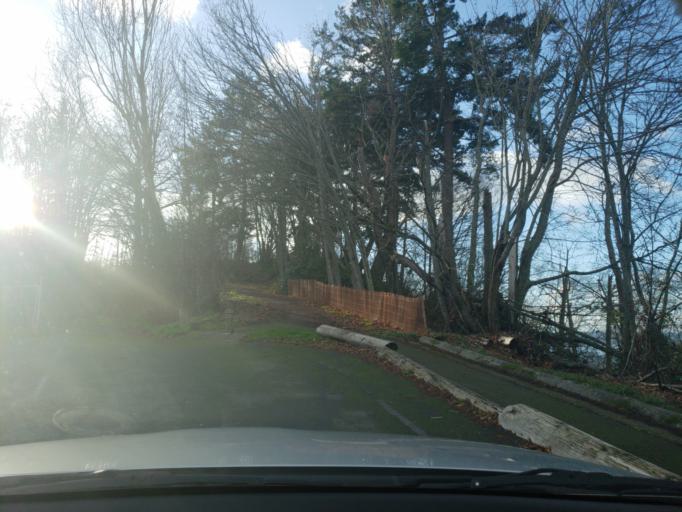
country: US
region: Washington
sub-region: King County
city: Seattle
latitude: 47.6683
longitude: -122.4186
